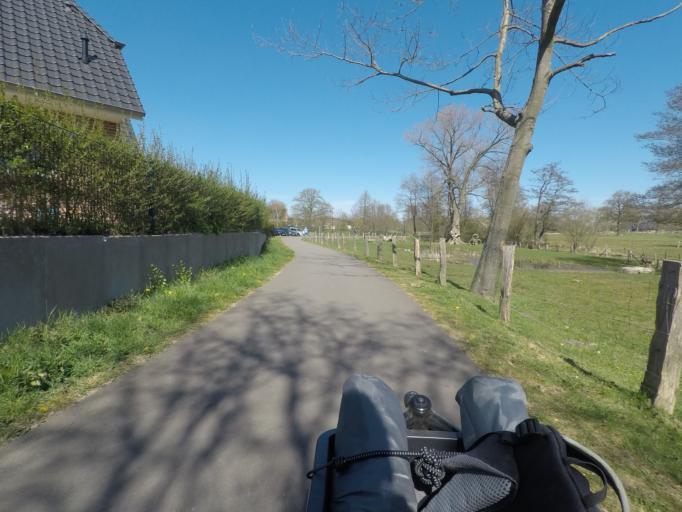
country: DE
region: Schleswig-Holstein
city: Stapelfeld
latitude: 53.5875
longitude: 10.2381
